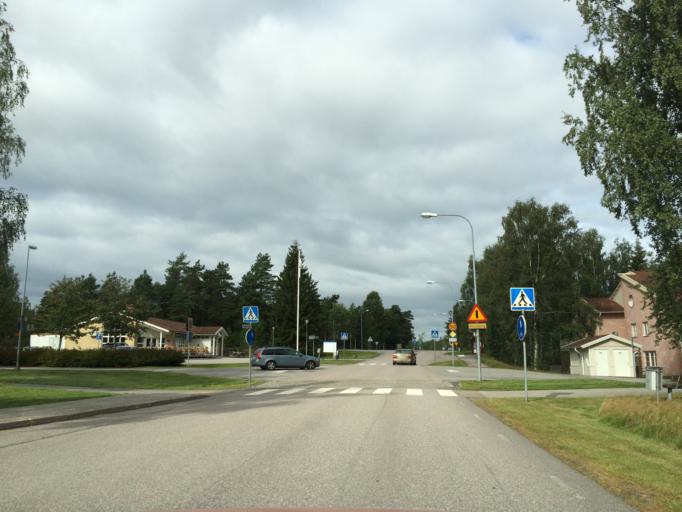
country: SE
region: Vaestra Goetaland
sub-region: Trollhattan
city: Trollhattan
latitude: 58.3193
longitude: 12.2735
